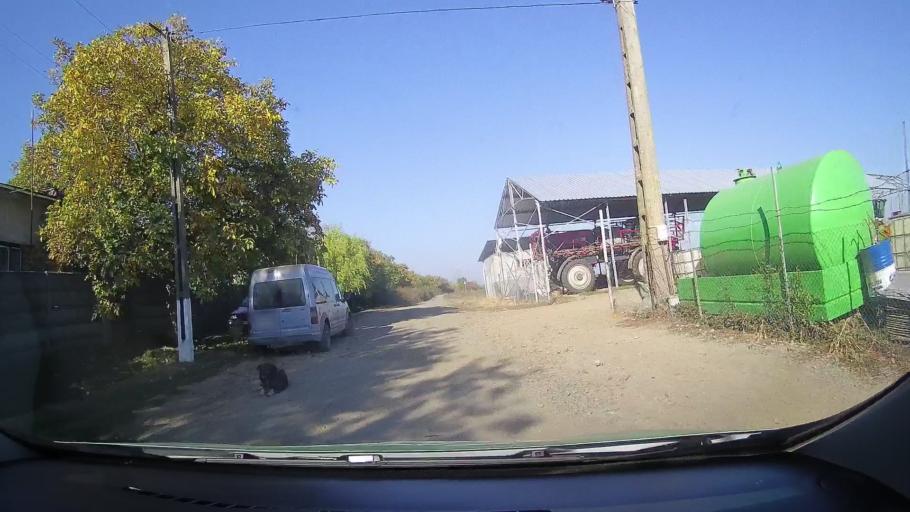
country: RO
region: Satu Mare
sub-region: Comuna Sauca
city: Sauca
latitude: 47.4724
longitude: 22.4844
